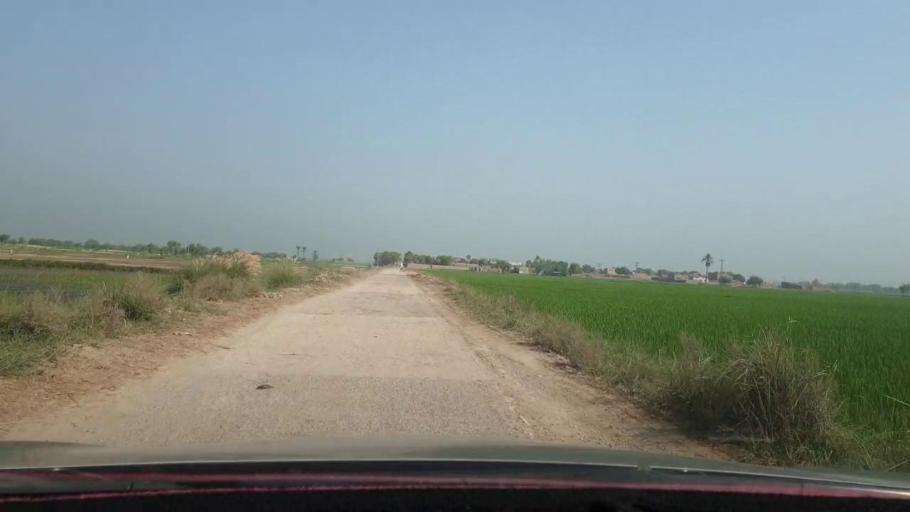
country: PK
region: Sindh
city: Kambar
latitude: 27.5986
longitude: 67.9366
